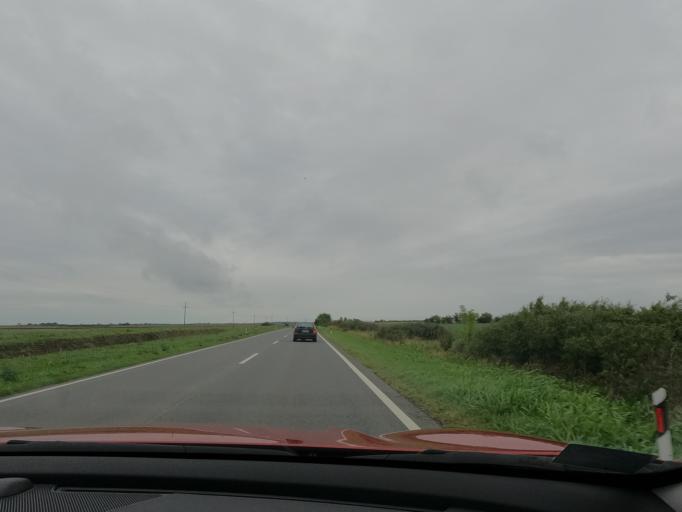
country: RS
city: Banatska Topola
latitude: 45.7077
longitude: 20.4188
